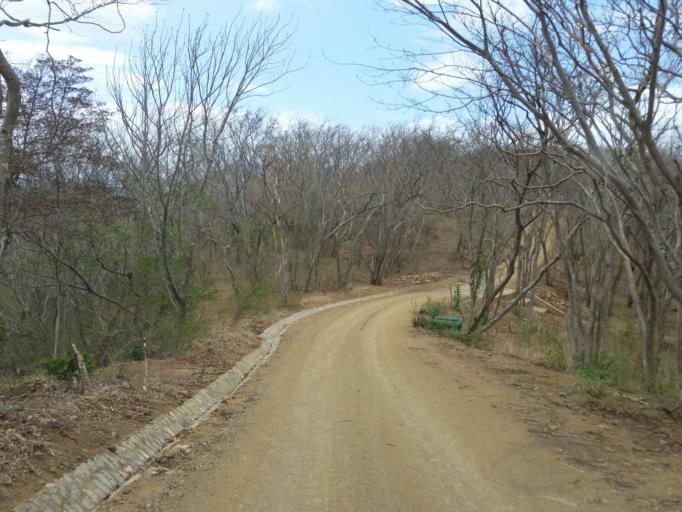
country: NI
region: Rivas
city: Tola
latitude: 11.4202
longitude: -86.0678
